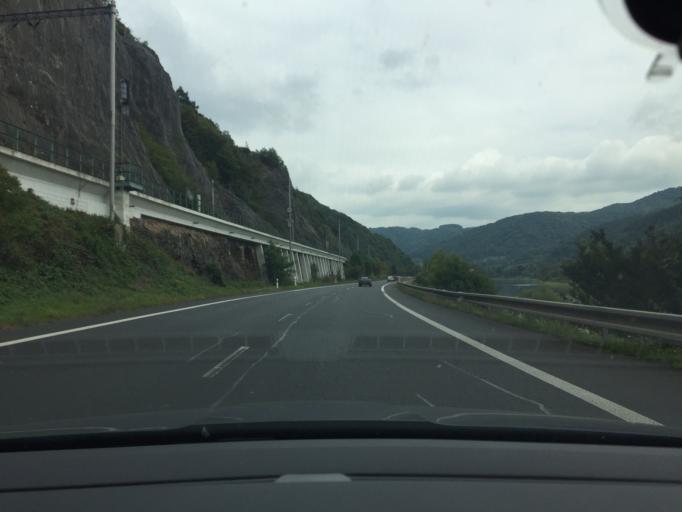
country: CZ
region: Ustecky
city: Povrly
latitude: 50.6831
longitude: 14.1709
